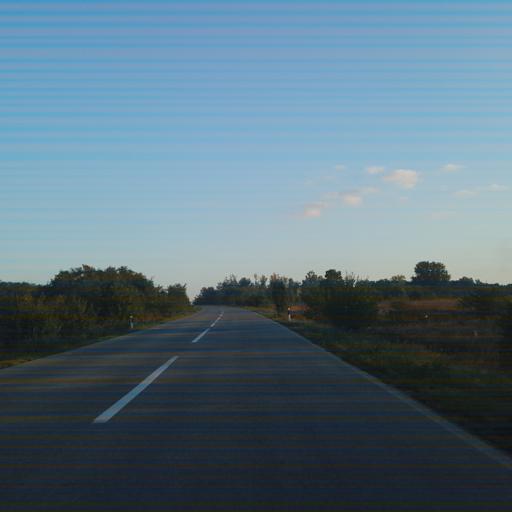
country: RS
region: Central Serbia
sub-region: Zajecarski Okrug
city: Zajecar
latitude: 44.0497
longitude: 22.3347
